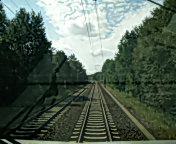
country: DE
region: Brandenburg
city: Halbe
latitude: 52.0553
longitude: 13.7218
